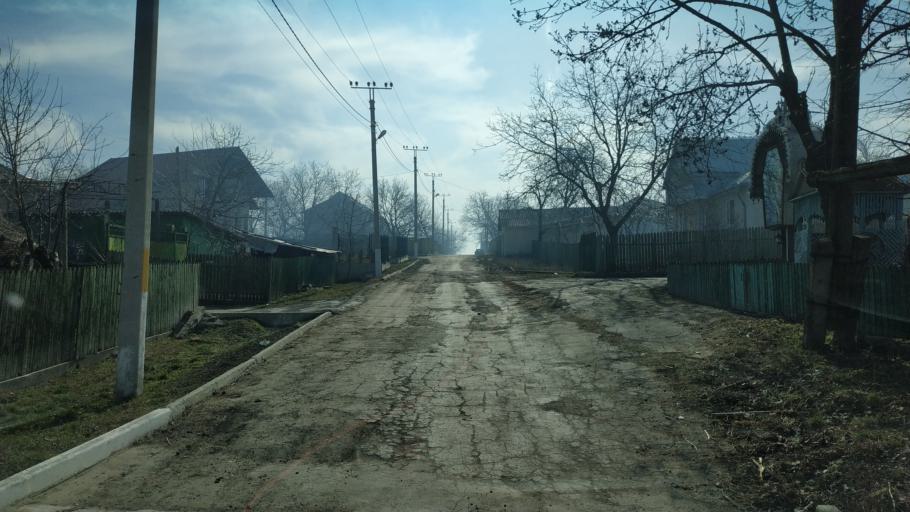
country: MD
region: Nisporeni
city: Nisporeni
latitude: 47.0752
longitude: 28.2639
